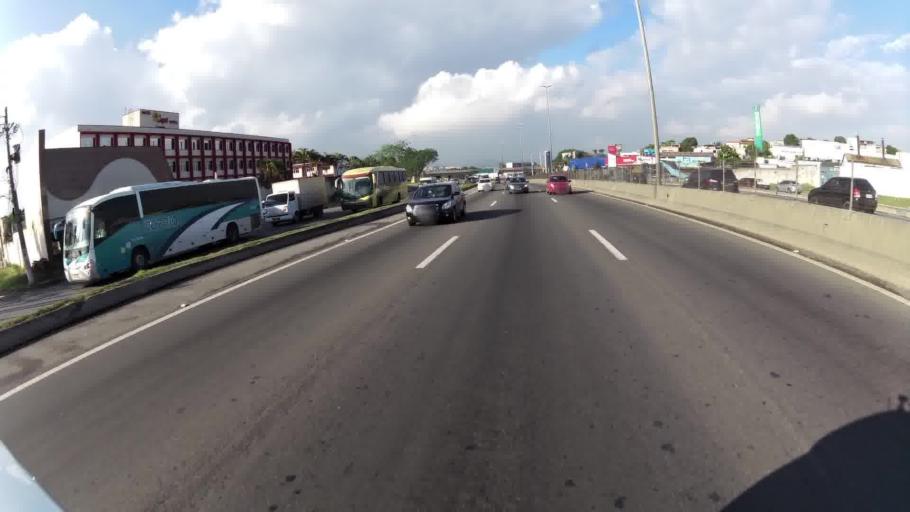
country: BR
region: Rio de Janeiro
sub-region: Duque De Caxias
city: Duque de Caxias
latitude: -22.7981
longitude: -43.2896
